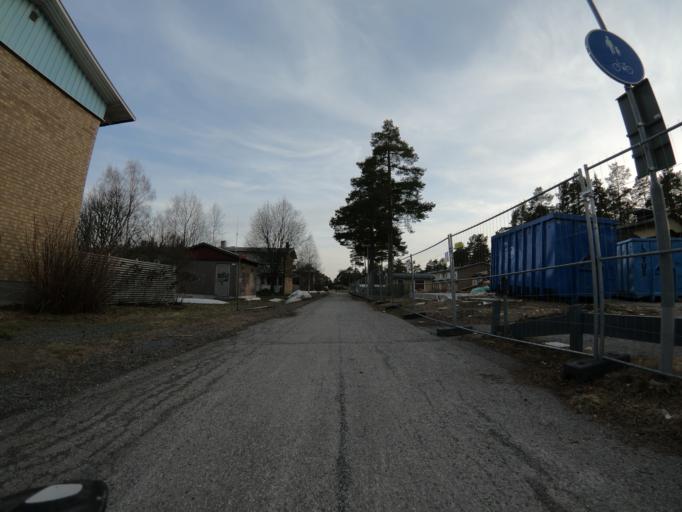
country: SE
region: Vaesterbotten
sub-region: Umea Kommun
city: Umea
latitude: 63.8427
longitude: 20.2826
